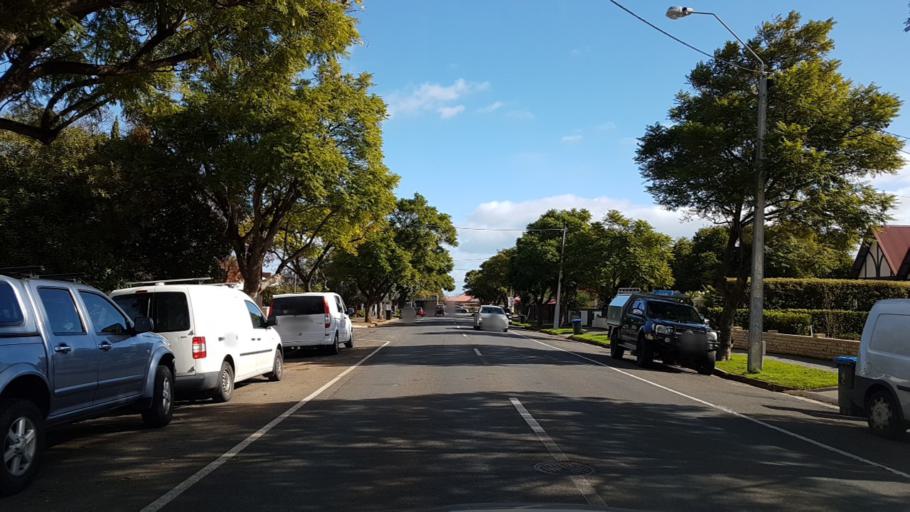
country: AU
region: South Australia
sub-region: Mitcham
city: Clarence Gardens
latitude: -34.9744
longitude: 138.5931
